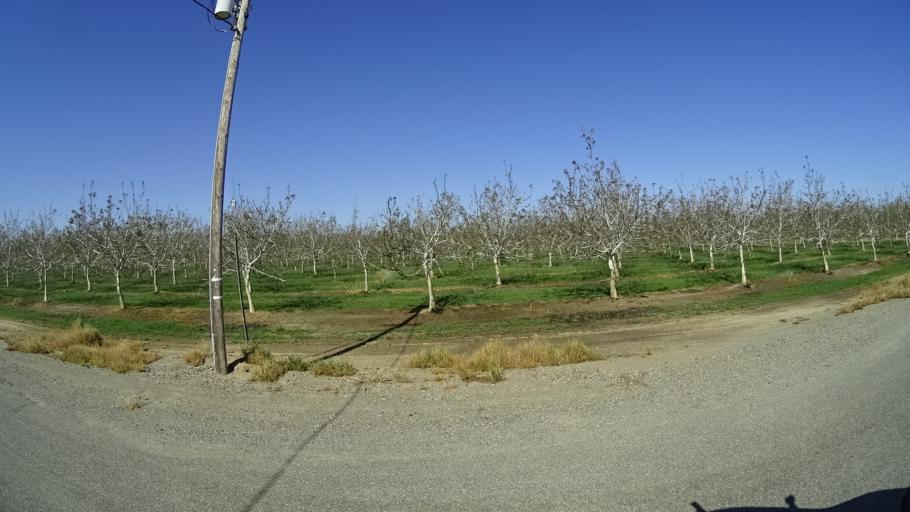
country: US
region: California
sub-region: Glenn County
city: Hamilton City
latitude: 39.6916
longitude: -122.0743
